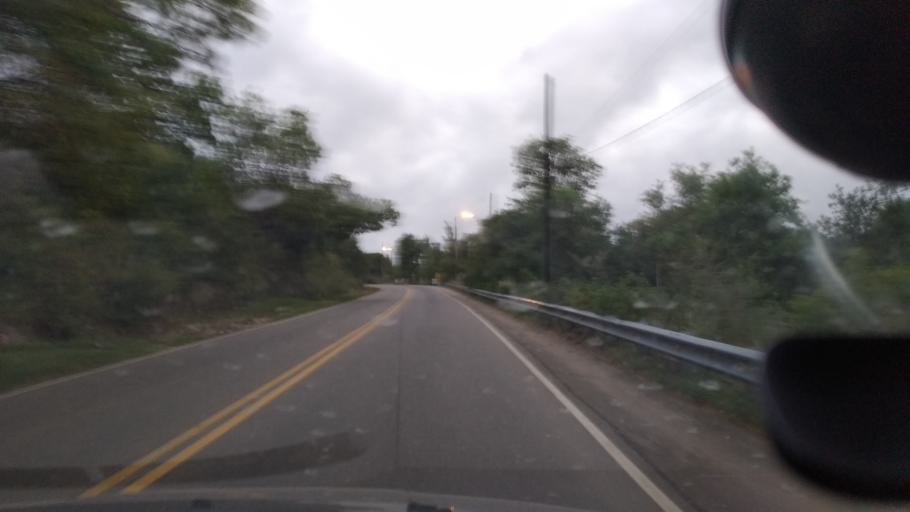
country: AR
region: Cordoba
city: Villa Las Rosas
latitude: -31.9240
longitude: -65.0398
